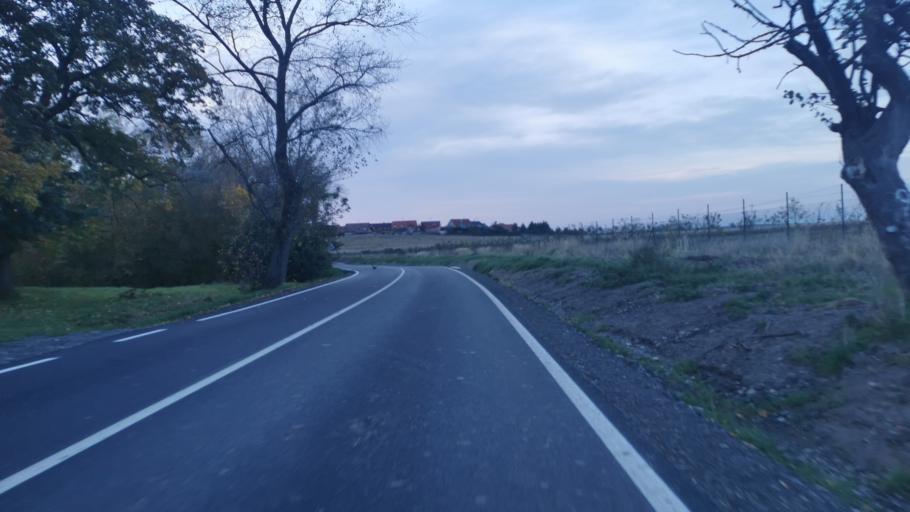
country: CZ
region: South Moravian
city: Sudomerice
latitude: 48.8478
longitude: 17.2482
